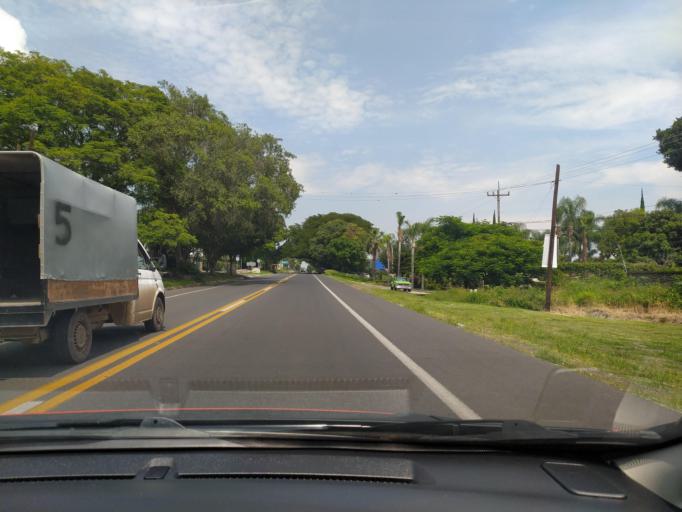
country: MX
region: Jalisco
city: San Juan Cosala
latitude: 20.2931
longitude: -103.3754
